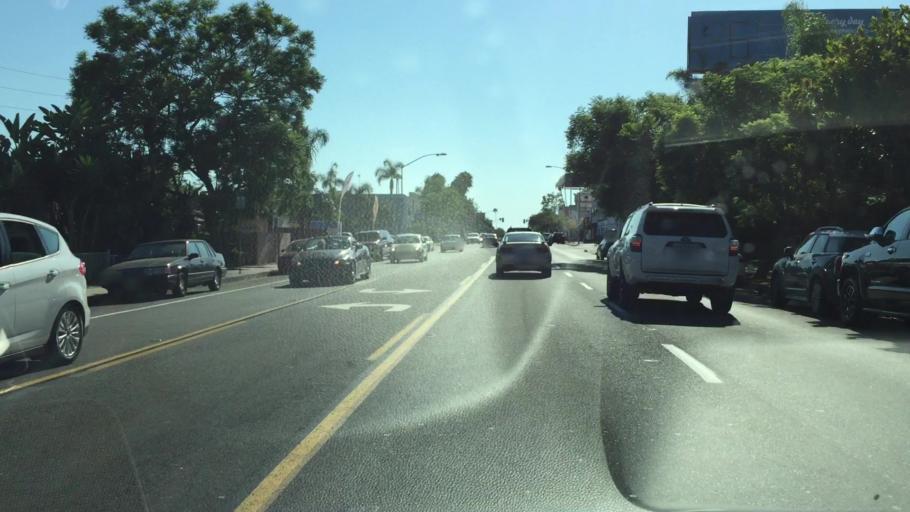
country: US
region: California
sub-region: San Diego County
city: La Jolla
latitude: 32.8017
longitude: -117.2325
